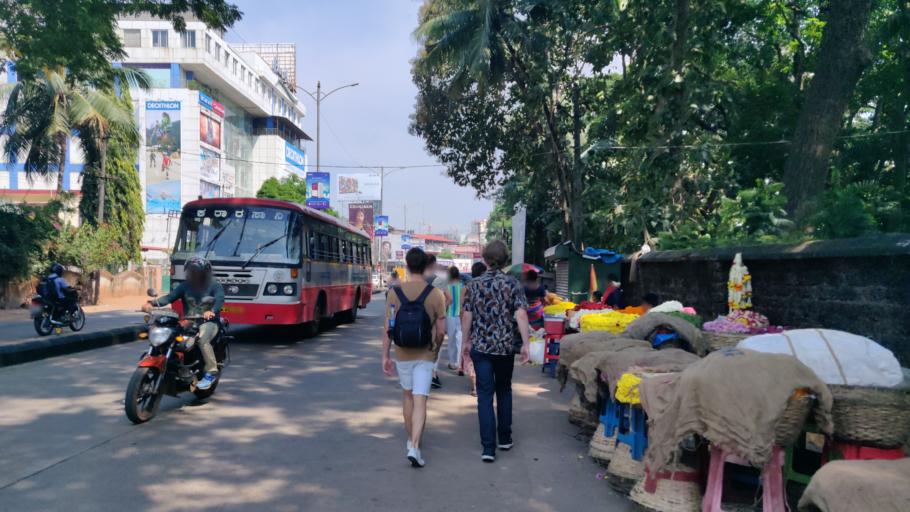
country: IN
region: Karnataka
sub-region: Dakshina Kannada
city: Mangalore
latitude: 12.8855
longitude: 74.8400
